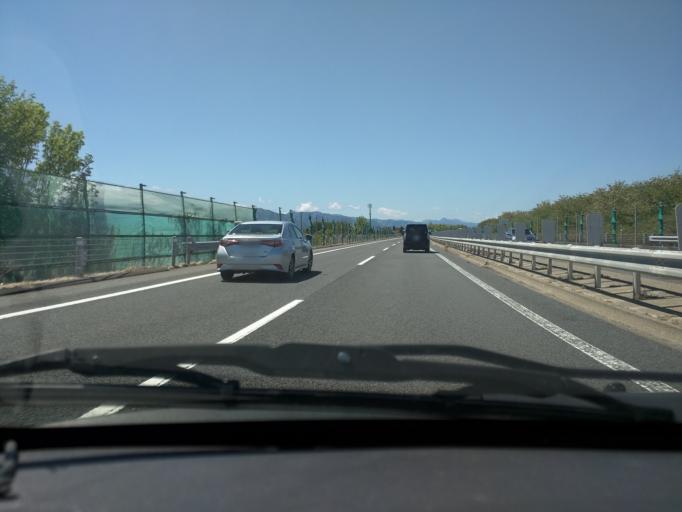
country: JP
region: Nagano
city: Suzaka
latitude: 36.7096
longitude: 138.3082
